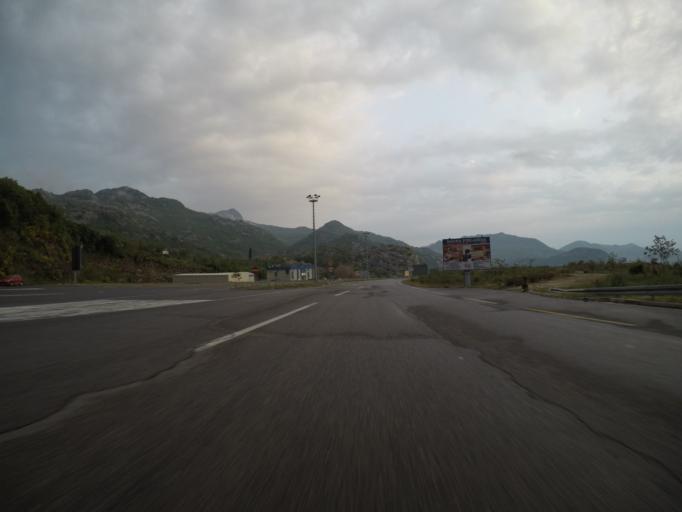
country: ME
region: Bar
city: Sutomore
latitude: 42.2018
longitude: 19.0513
